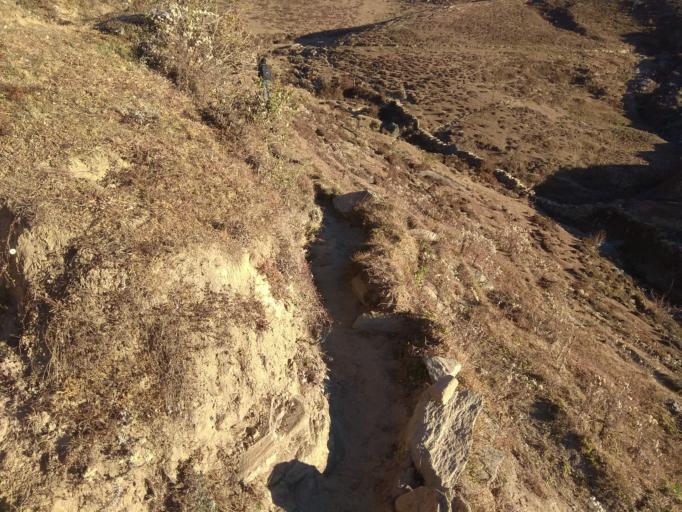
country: NP
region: Far Western
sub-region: Seti Zone
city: Achham
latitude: 29.2748
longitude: 81.6459
